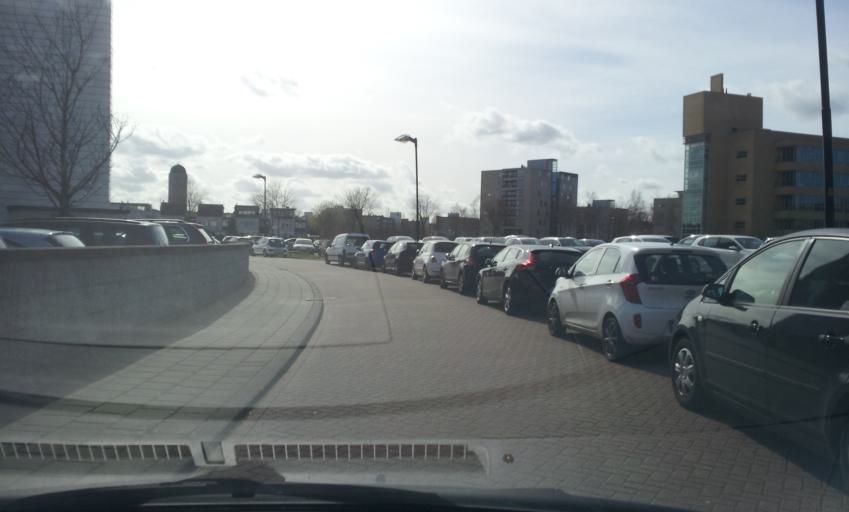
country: NL
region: South Holland
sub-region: Gemeente Zoetermeer
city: Zoetermeer
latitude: 52.0456
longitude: 4.4828
